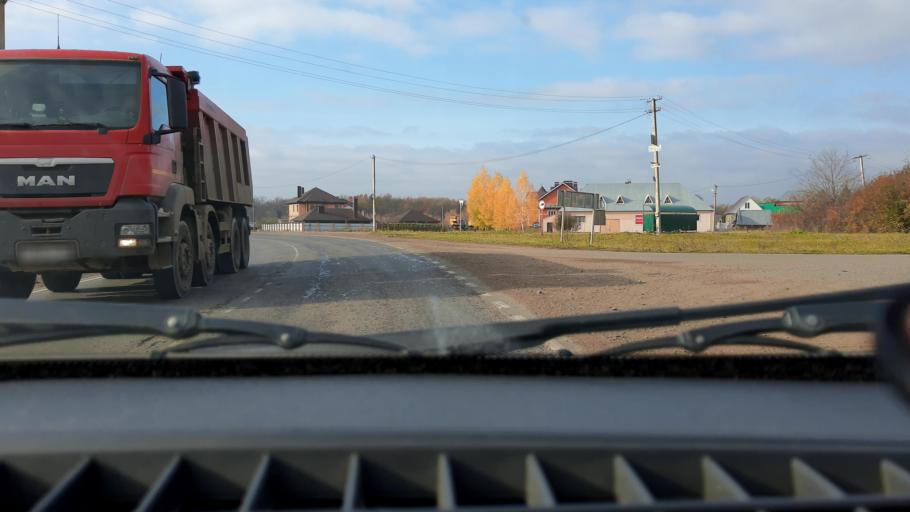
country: RU
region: Bashkortostan
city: Ufa
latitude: 54.5701
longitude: 55.9659
